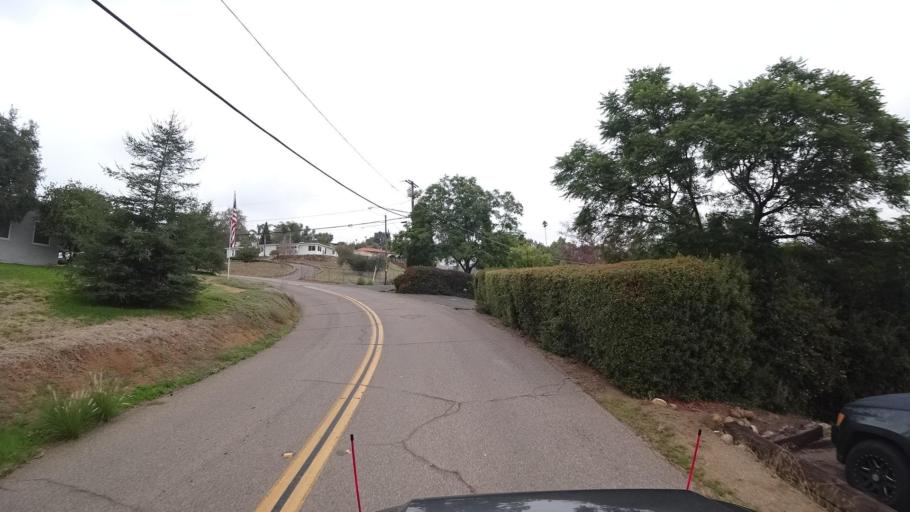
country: US
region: California
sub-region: San Diego County
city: Spring Valley
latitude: 32.7472
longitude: -117.0061
